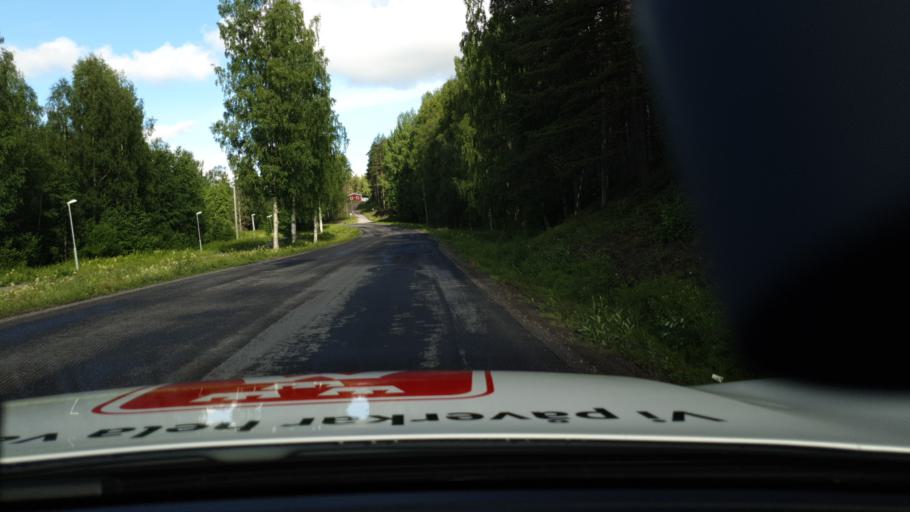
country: SE
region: Norrbotten
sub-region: Bodens Kommun
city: Boden
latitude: 65.8312
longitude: 21.6240
